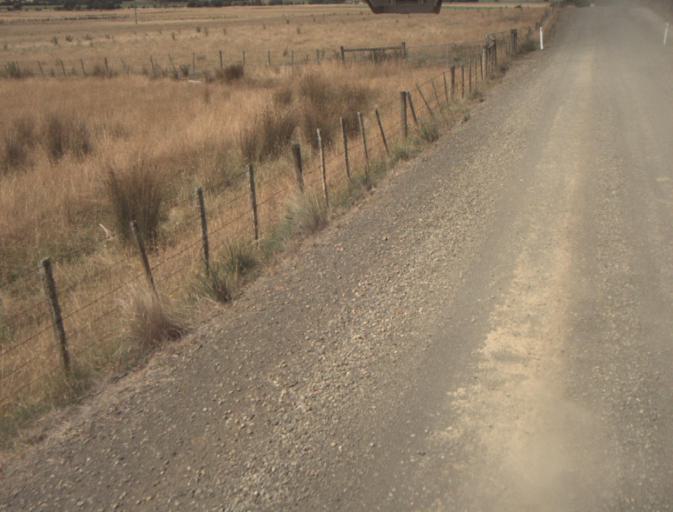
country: AU
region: Tasmania
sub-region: Northern Midlands
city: Evandale
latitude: -41.4732
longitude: 147.4461
